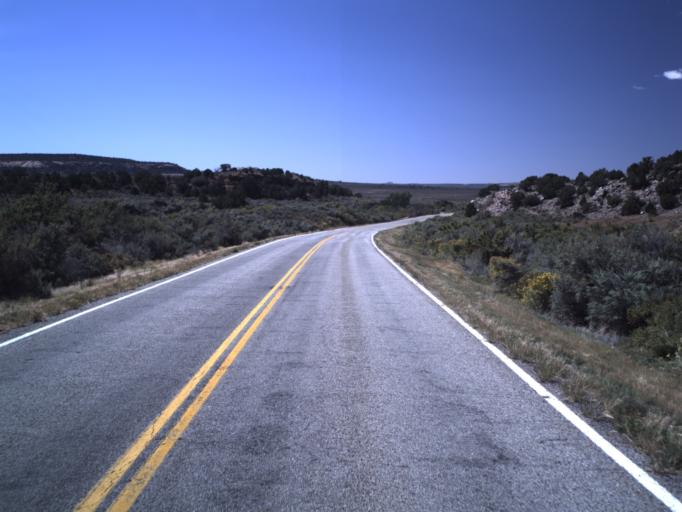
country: US
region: Utah
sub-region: Grand County
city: Moab
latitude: 38.3072
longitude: -109.3607
